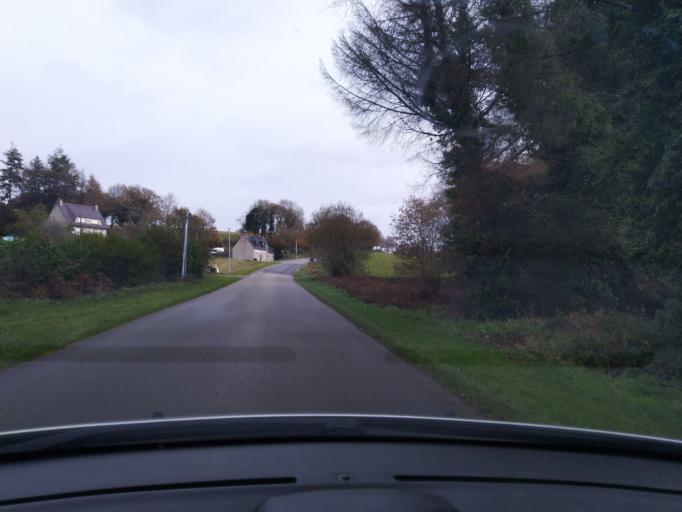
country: FR
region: Brittany
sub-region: Departement du Finistere
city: Guerlesquin
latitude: 48.5230
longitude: -3.5775
